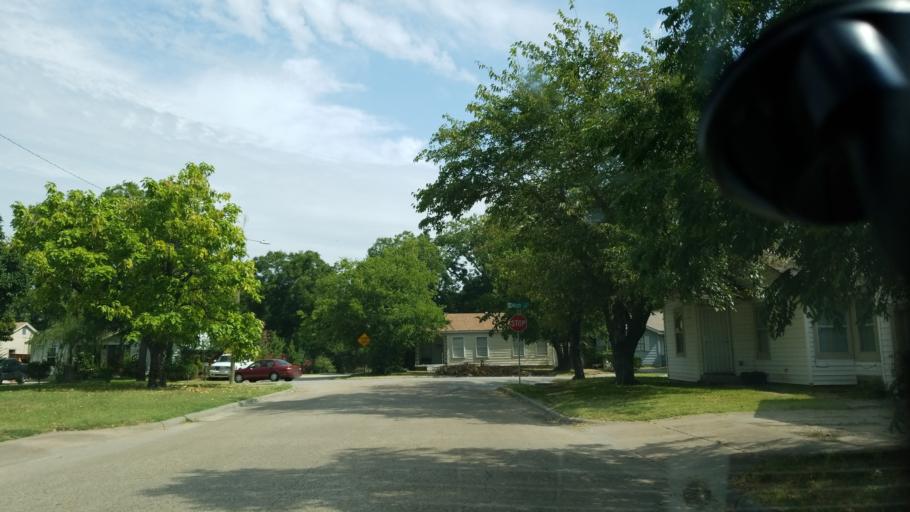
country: US
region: Texas
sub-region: Dallas County
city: Grand Prairie
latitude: 32.7513
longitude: -96.9924
